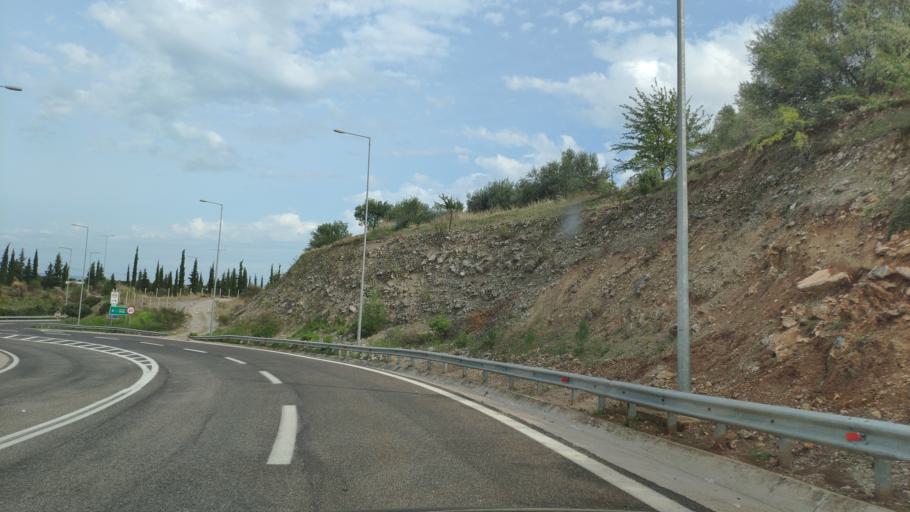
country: GR
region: Central Greece
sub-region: Nomos Fthiotidos
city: Anthili
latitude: 38.7977
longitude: 22.5113
